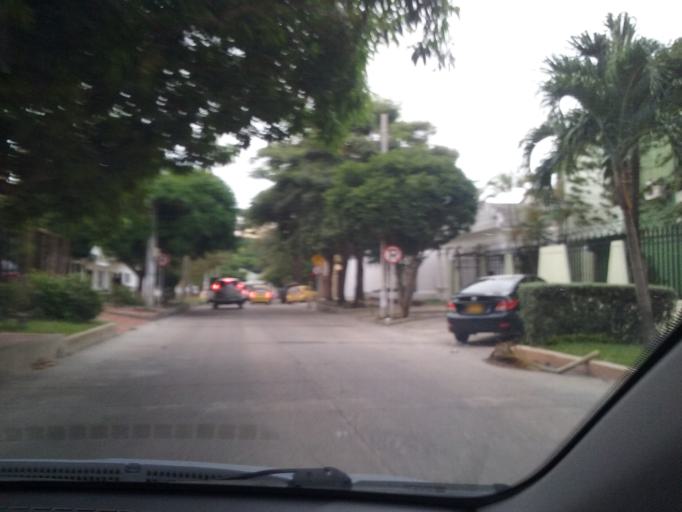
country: CO
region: Atlantico
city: Barranquilla
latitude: 10.9929
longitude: -74.7980
